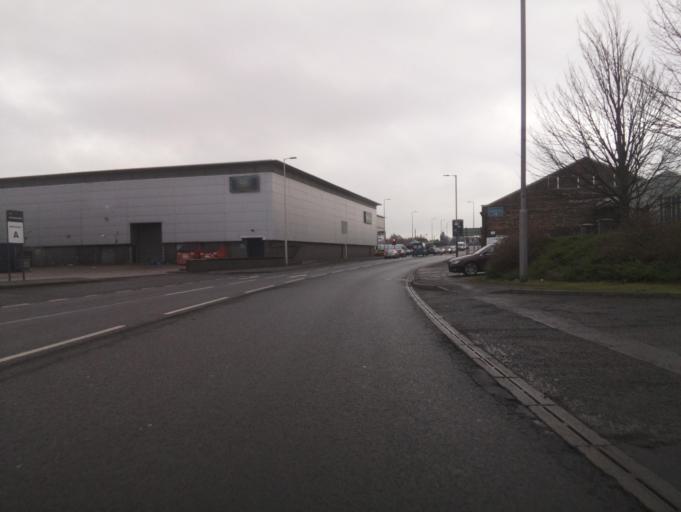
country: GB
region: Scotland
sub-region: Dundee City
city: Dundee
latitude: 56.4813
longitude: -2.9984
